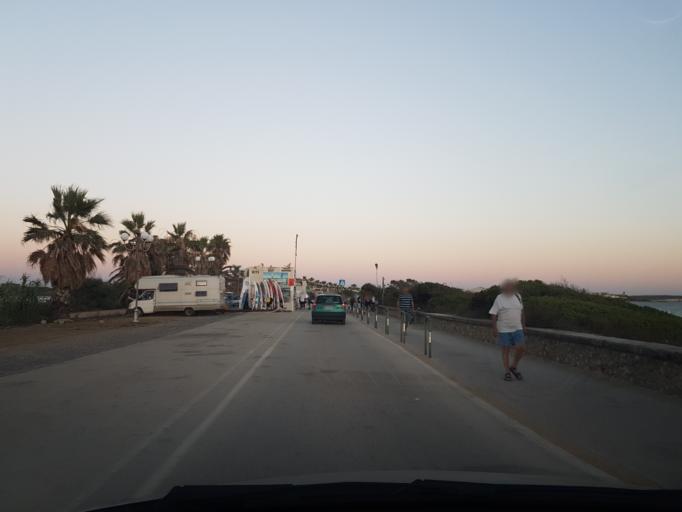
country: IT
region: Sardinia
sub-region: Provincia di Oristano
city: Riola Sardo
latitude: 40.0322
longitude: 8.4030
